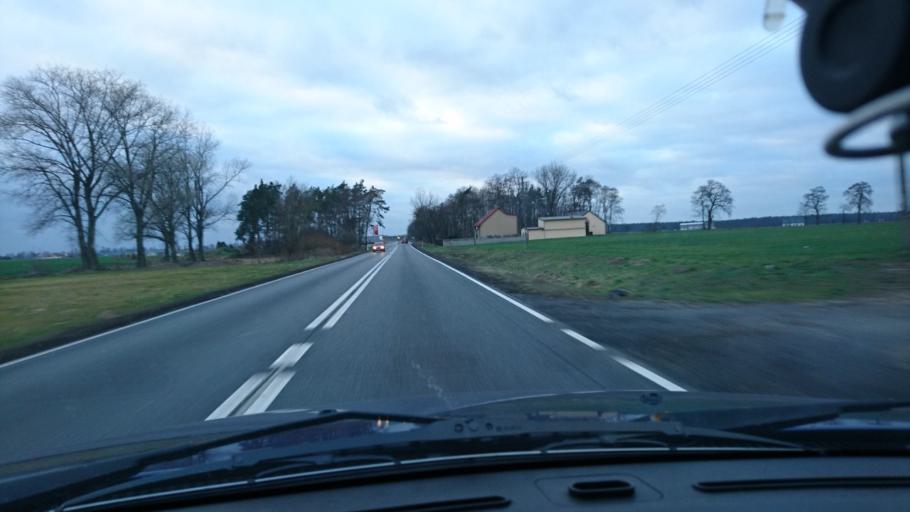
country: PL
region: Greater Poland Voivodeship
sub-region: Powiat kepinski
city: Leka Opatowska
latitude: 51.2229
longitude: 18.1191
